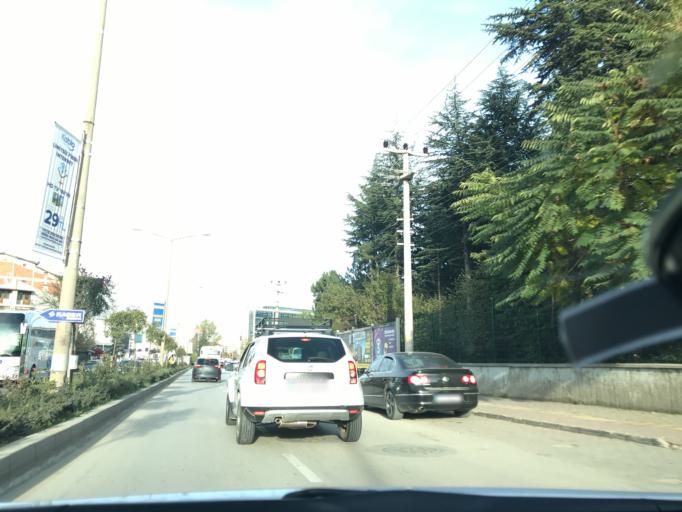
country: TR
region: Bolu
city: Bolu
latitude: 40.7361
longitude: 31.6180
